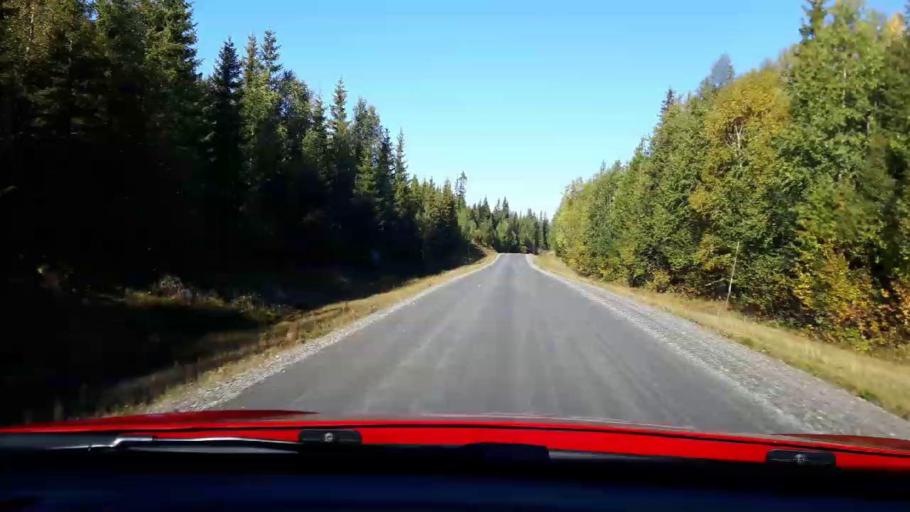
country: NO
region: Nord-Trondelag
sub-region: Lierne
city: Sandvika
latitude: 64.5294
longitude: 14.0458
